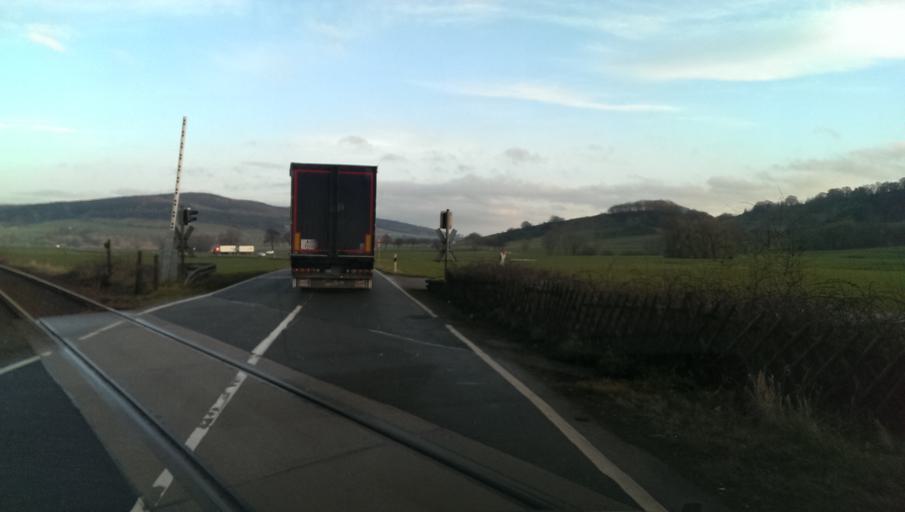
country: DE
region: Lower Saxony
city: Wangelnstedt
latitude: 51.8786
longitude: 9.6603
